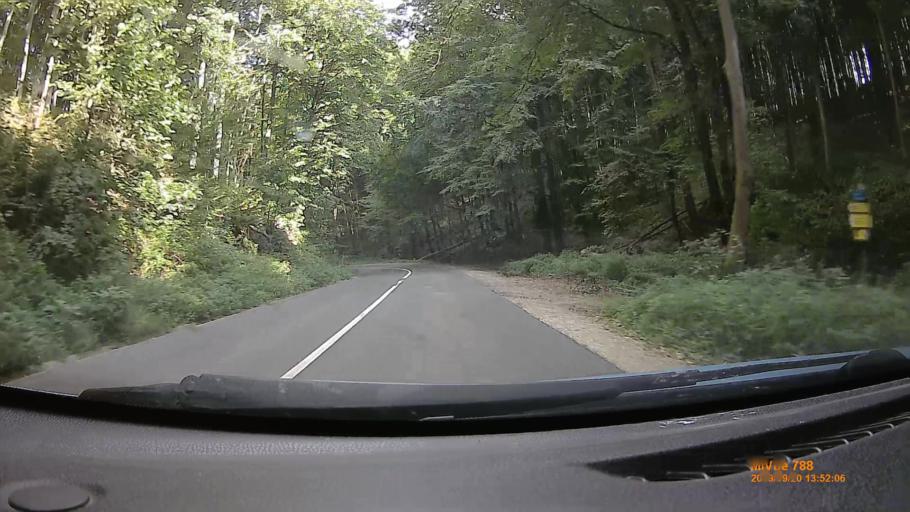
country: HU
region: Borsod-Abauj-Zemplen
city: Saly
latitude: 48.0706
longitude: 20.6020
